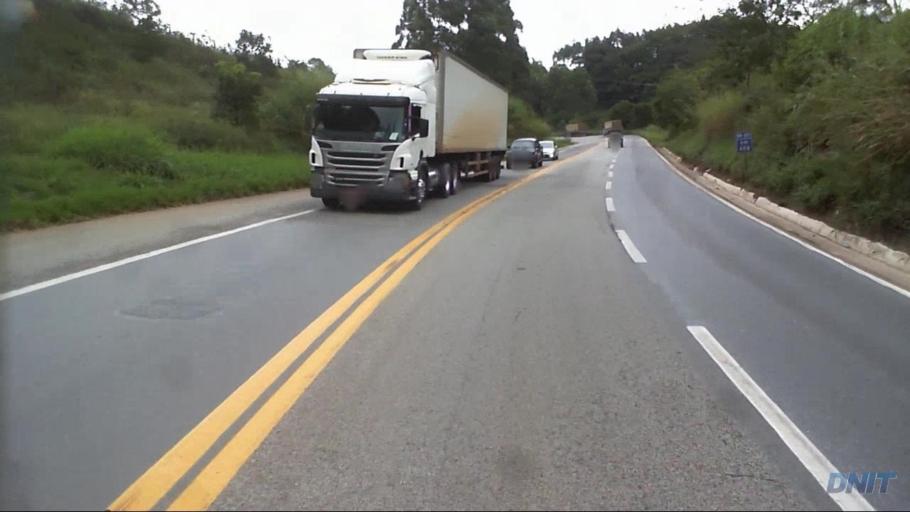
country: BR
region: Minas Gerais
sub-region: Caete
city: Caete
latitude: -19.7524
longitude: -43.5344
